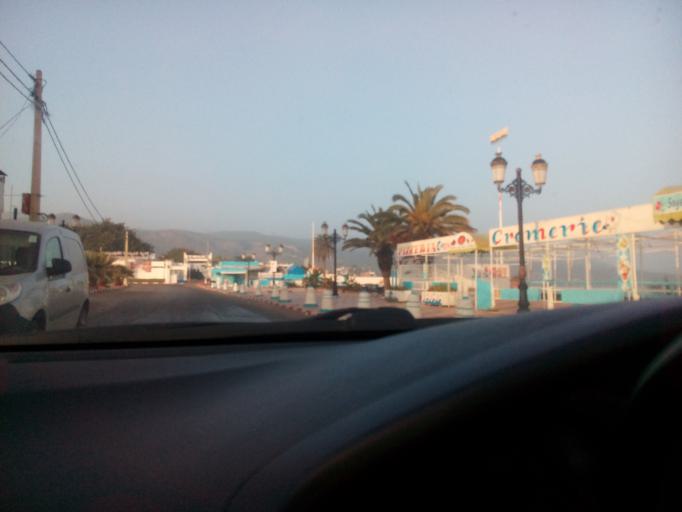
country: DZ
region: Oran
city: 'Ain el Turk
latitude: 35.7056
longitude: -0.8915
